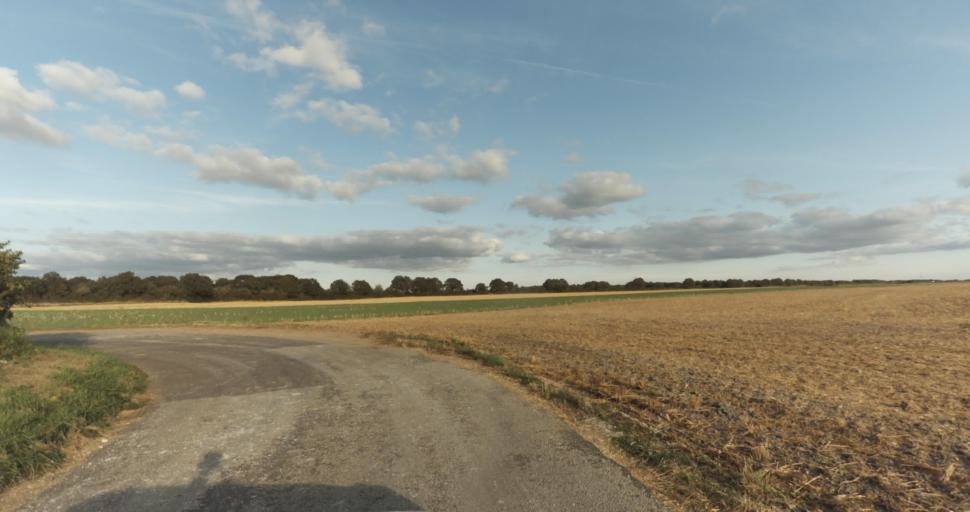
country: FR
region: Haute-Normandie
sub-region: Departement de l'Eure
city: Marcilly-sur-Eure
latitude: 48.8919
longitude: 1.2731
